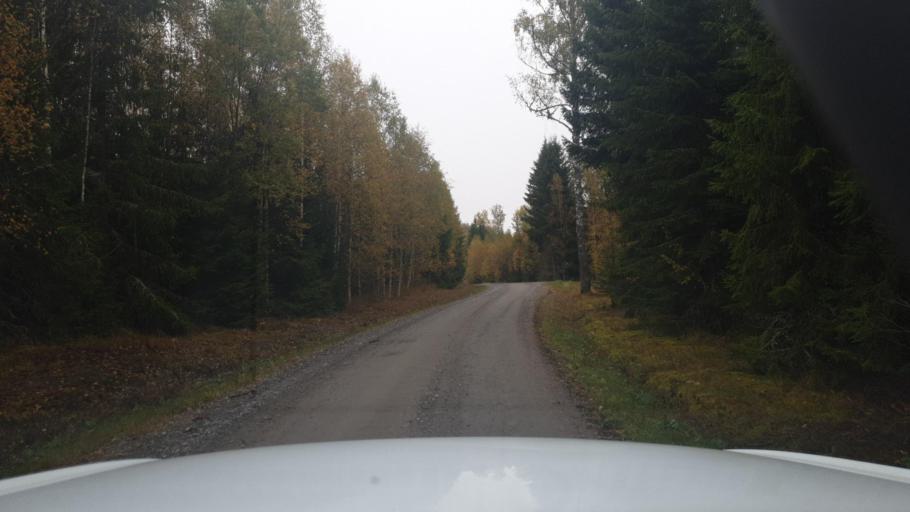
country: SE
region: Vaermland
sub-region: Karlstads Kommun
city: Edsvalla
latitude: 59.4667
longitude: 13.1239
